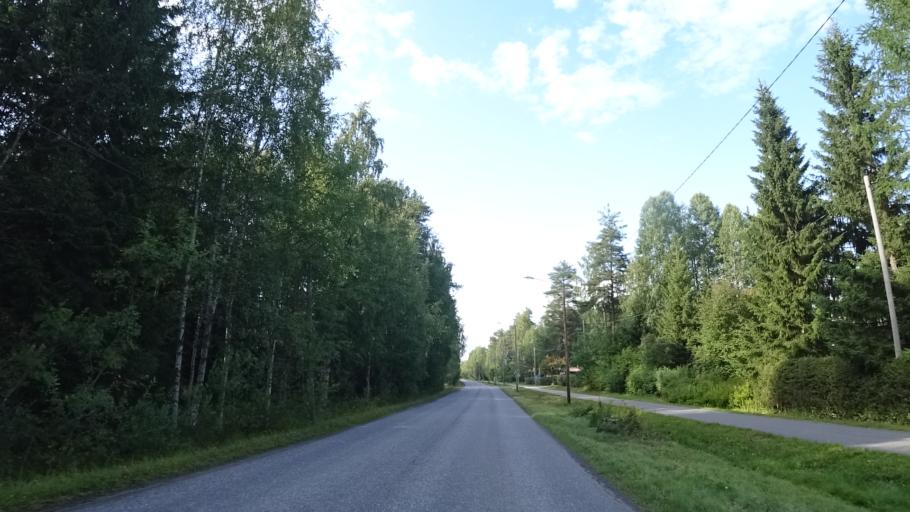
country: FI
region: North Karelia
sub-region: Pielisen Karjala
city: Lieksa
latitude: 63.3333
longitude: 30.0295
